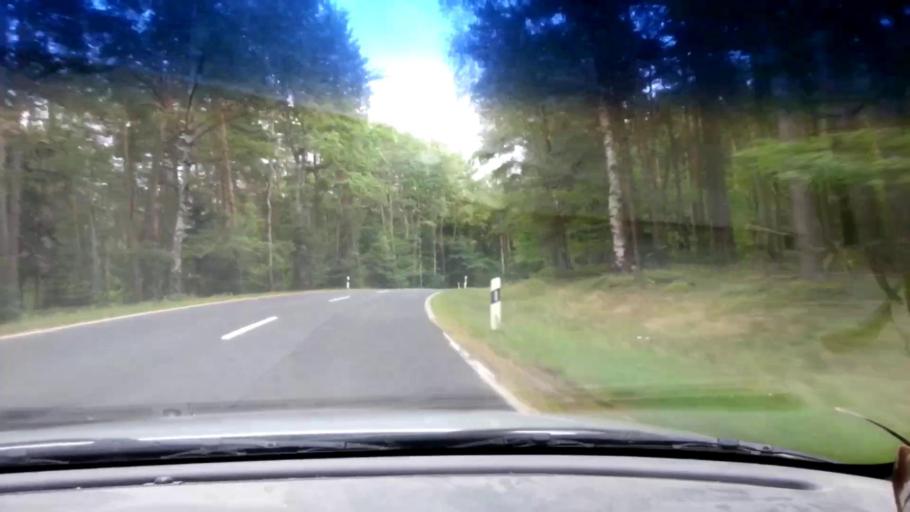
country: DE
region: Bavaria
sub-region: Upper Palatinate
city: Waldsassen
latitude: 50.0275
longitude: 12.3076
